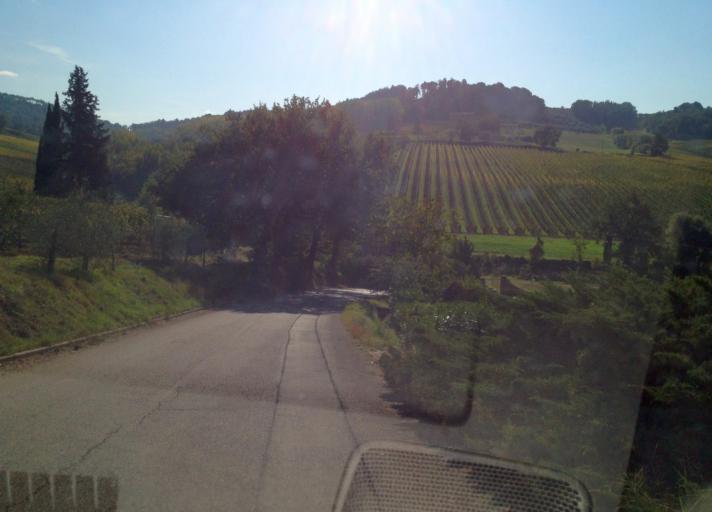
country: IT
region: Tuscany
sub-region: Provincia di Siena
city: Poggibonsi
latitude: 43.4900
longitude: 11.1776
